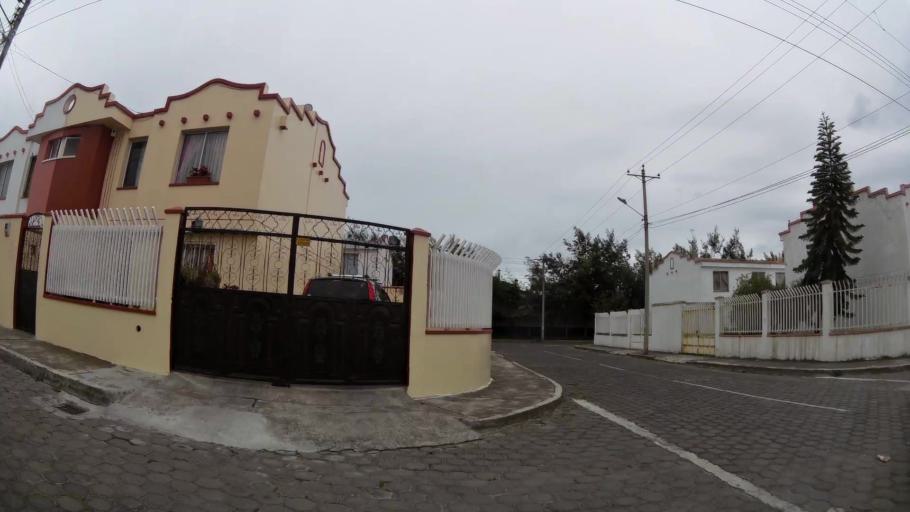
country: EC
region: Cotopaxi
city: Latacunga
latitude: -0.9420
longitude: -78.6095
